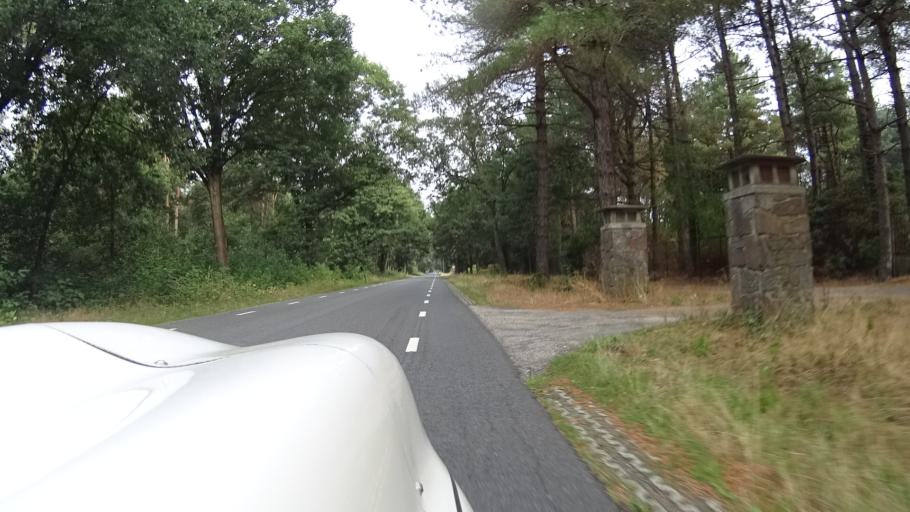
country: NL
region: North Brabant
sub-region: Gemeente Boxmeer
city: Overloon
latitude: 51.5887
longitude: 5.9299
